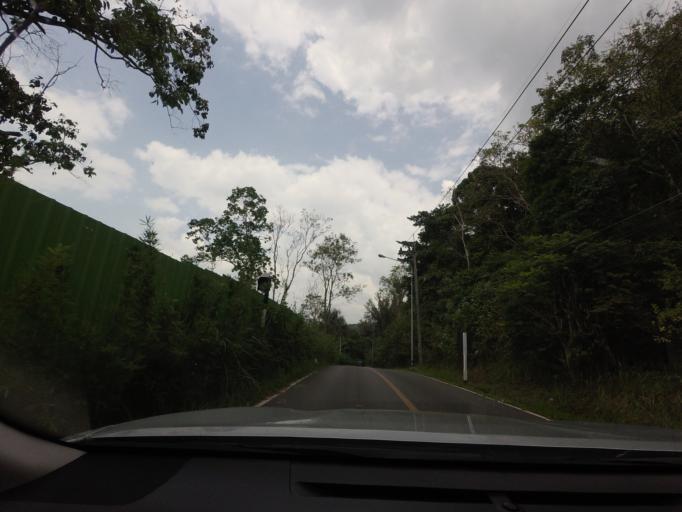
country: TH
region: Phangnga
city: Ban Ao Nang
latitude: 8.0869
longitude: 98.7459
